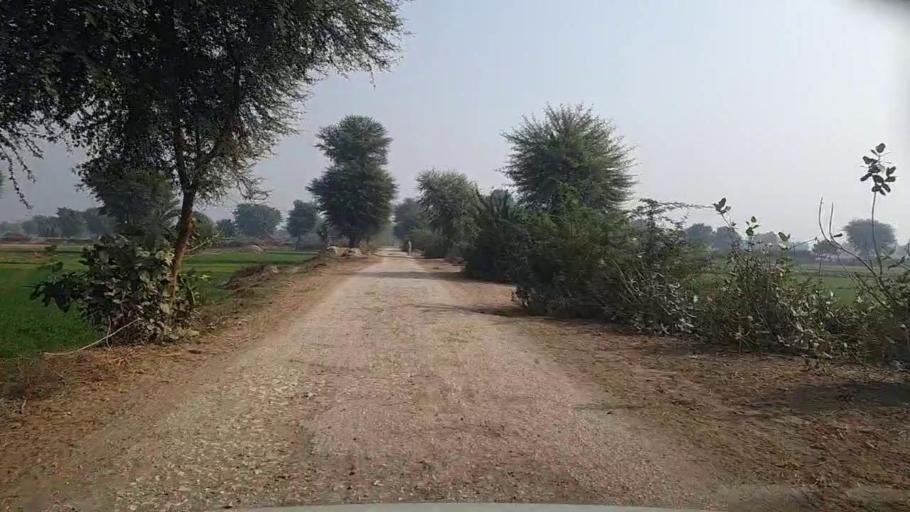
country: PK
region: Sindh
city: Setharja Old
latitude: 27.1412
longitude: 68.4956
